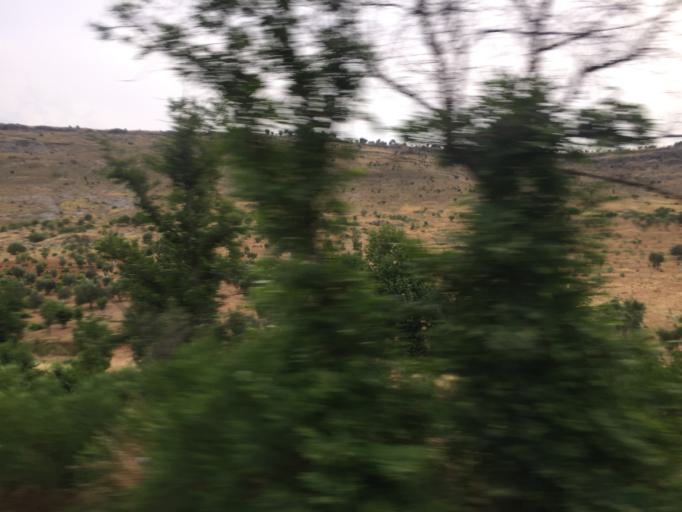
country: TR
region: Gaziantep
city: Yesildere
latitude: 36.9952
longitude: 37.4426
